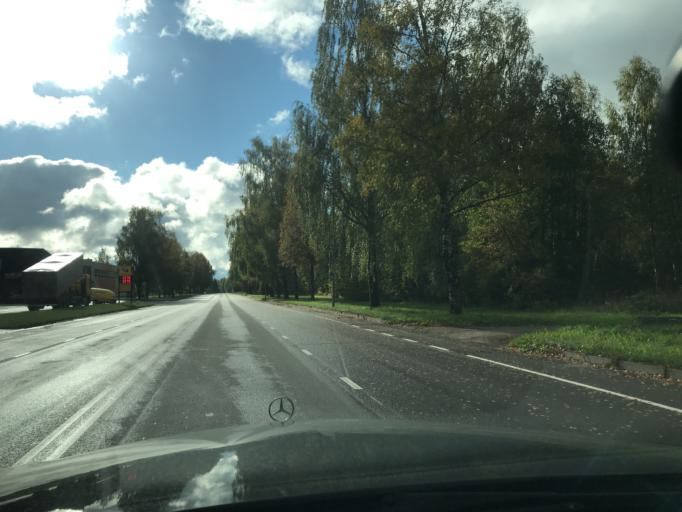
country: EE
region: Valgamaa
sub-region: Torva linn
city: Torva
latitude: 57.9914
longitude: 25.9390
